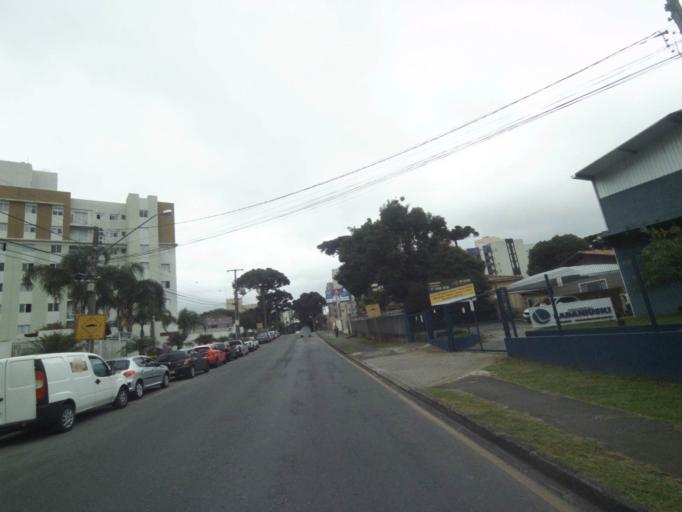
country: BR
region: Parana
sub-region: Curitiba
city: Curitiba
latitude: -25.4943
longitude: -49.2889
